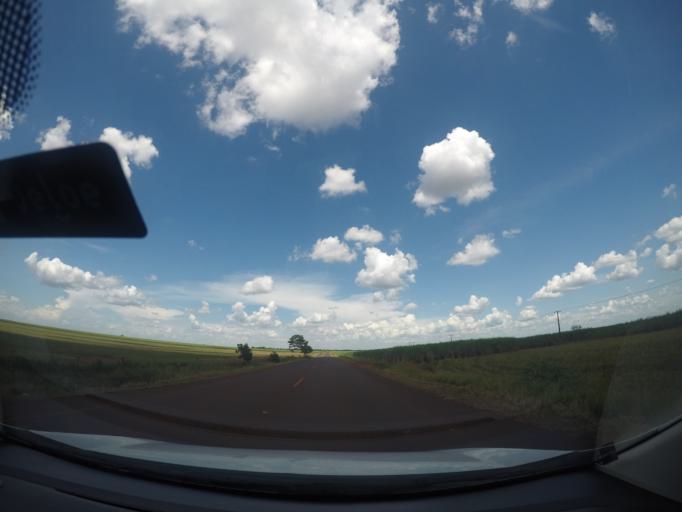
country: BR
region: Minas Gerais
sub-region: Frutal
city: Frutal
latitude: -19.9229
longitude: -48.6739
